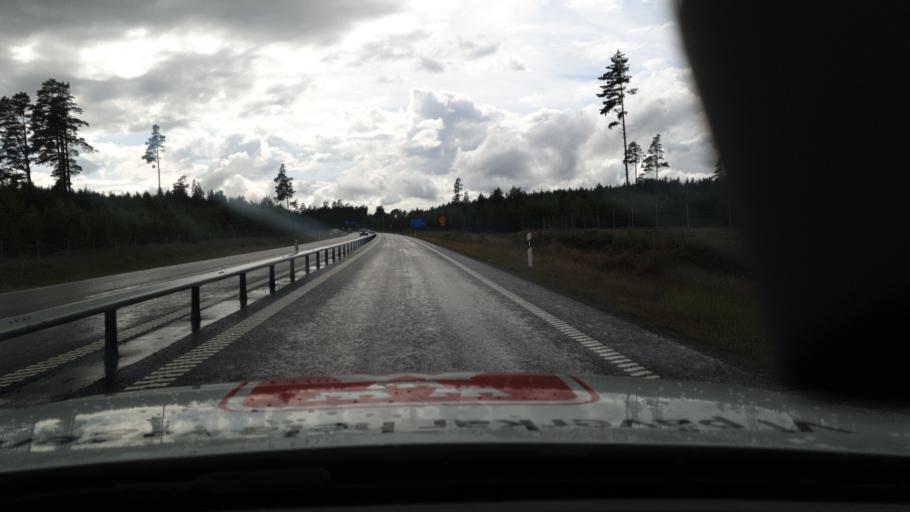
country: SE
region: Vaestra Goetaland
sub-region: Lidkopings Kommun
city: Lidkoping
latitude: 58.4794
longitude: 13.2116
